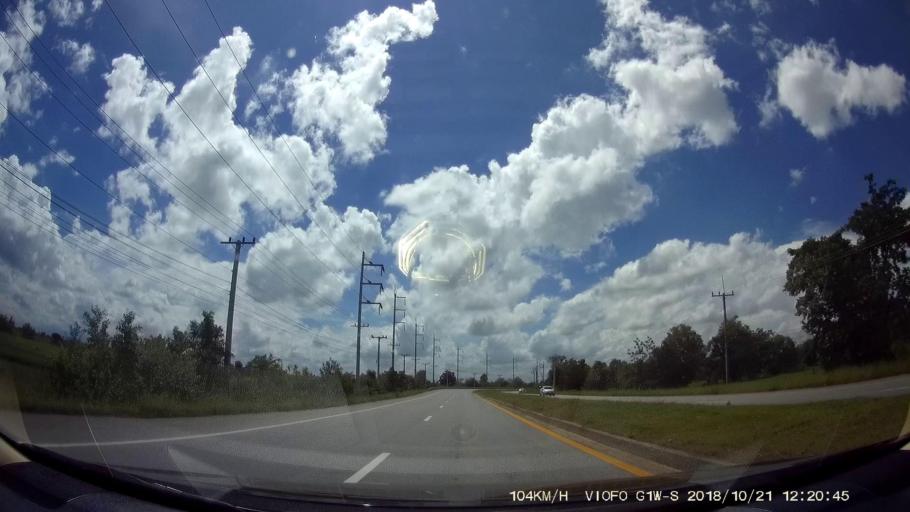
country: TH
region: Nakhon Ratchasima
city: Dan Khun Thot
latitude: 15.2839
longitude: 101.8003
